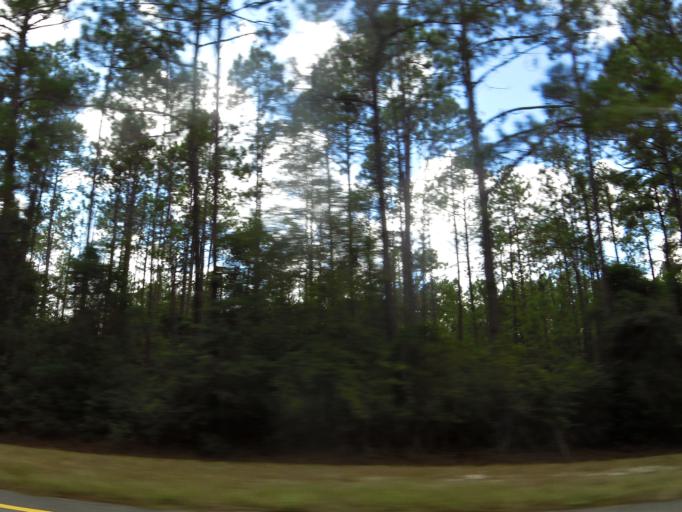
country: US
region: Georgia
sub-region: Charlton County
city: Folkston
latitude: 30.8743
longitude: -82.0132
